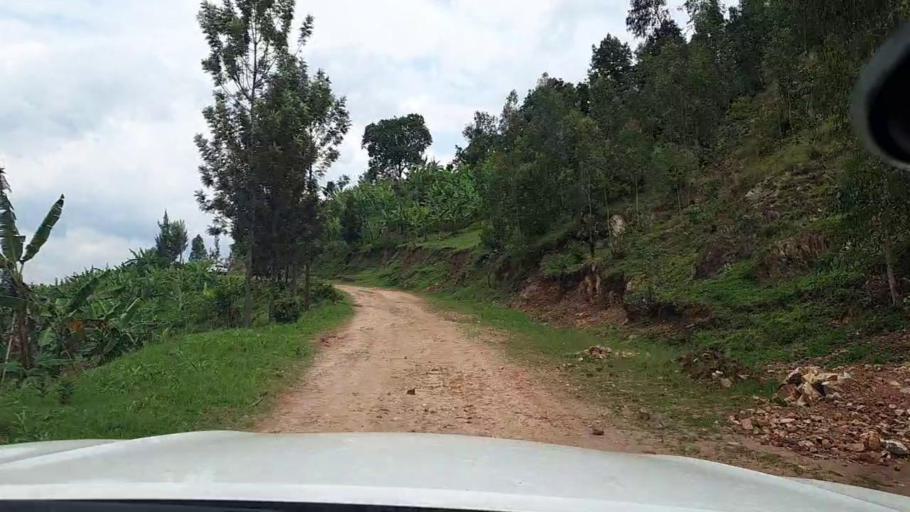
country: RW
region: Western Province
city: Kibuye
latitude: -2.0800
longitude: 29.4221
